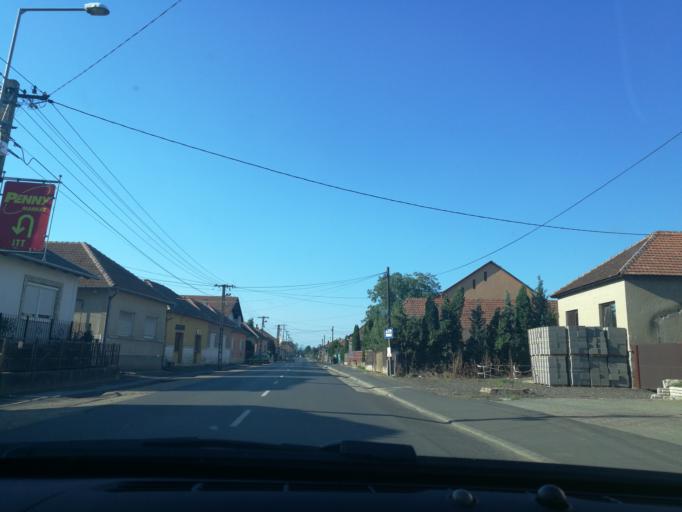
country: HU
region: Szabolcs-Szatmar-Bereg
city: Rakamaz
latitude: 48.1272
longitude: 21.4587
